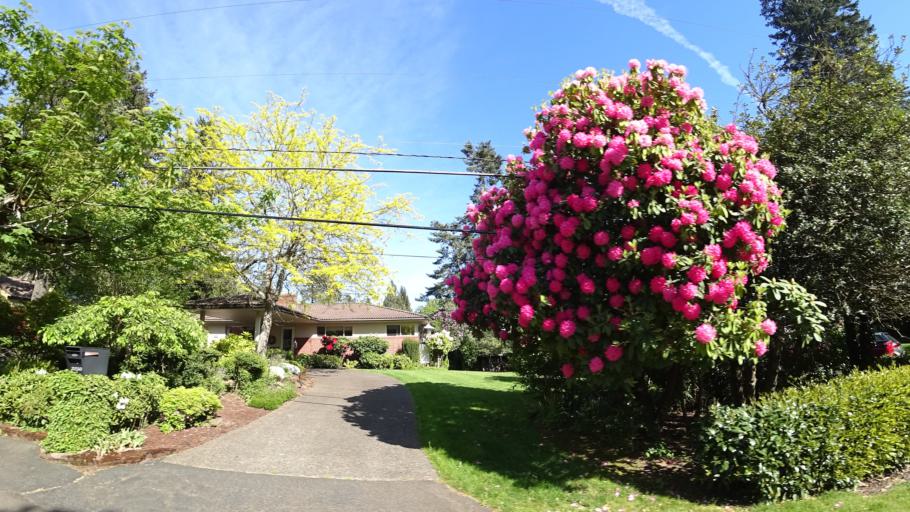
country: US
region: Oregon
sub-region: Washington County
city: West Slope
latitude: 45.4963
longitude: -122.7524
